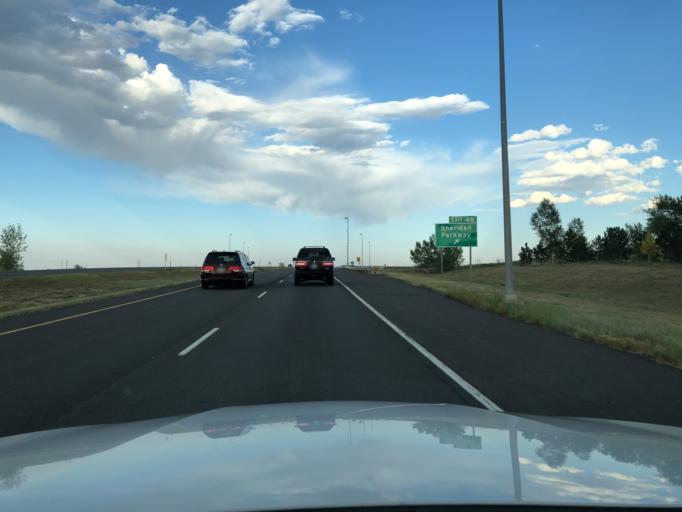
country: US
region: Colorado
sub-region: Boulder County
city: Lafayette
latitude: 39.9831
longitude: -105.0275
